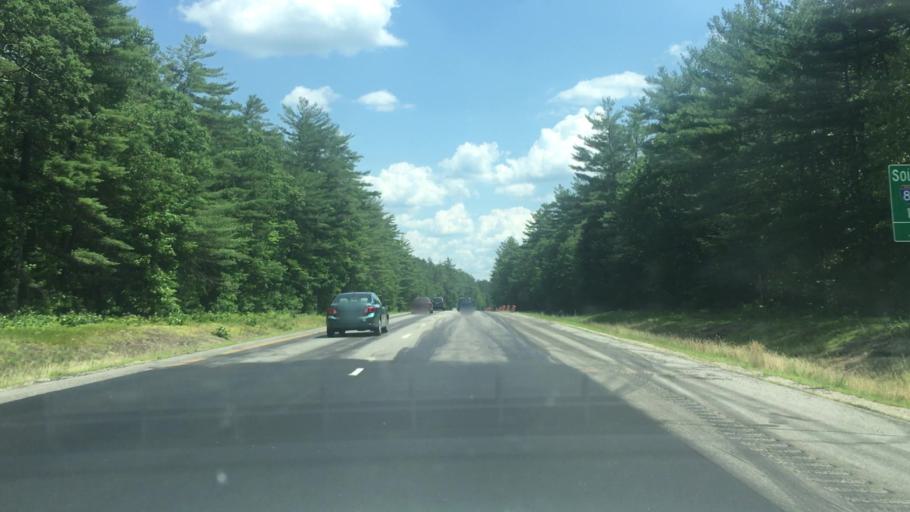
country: US
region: New Hampshire
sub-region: Merrimack County
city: Contoocook
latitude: 43.2635
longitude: -71.7630
